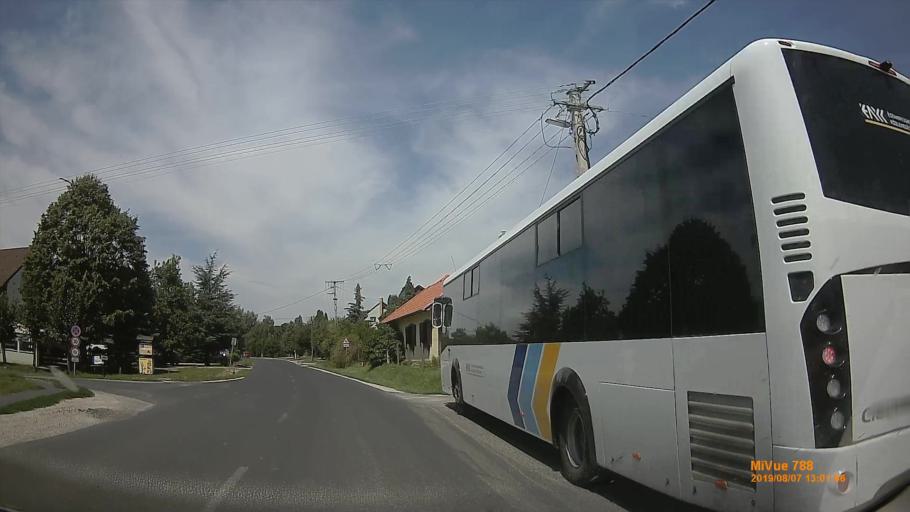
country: HU
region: Zala
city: Cserszegtomaj
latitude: 46.8060
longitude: 17.2315
